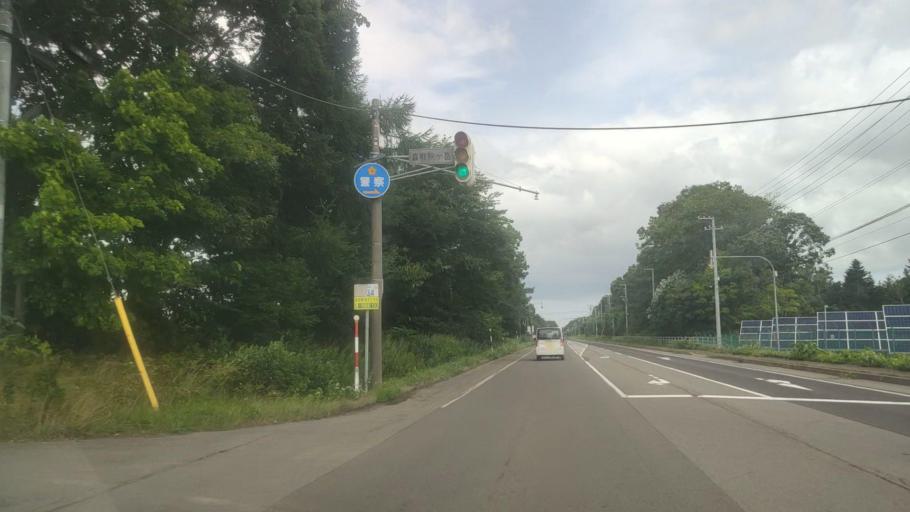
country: JP
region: Hokkaido
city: Nanae
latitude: 42.0367
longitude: 140.6069
